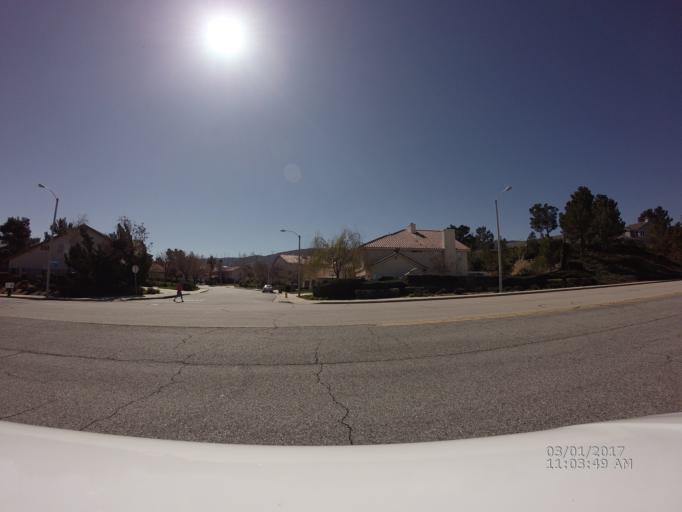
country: US
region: California
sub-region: Los Angeles County
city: Quartz Hill
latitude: 34.6456
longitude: -118.2582
